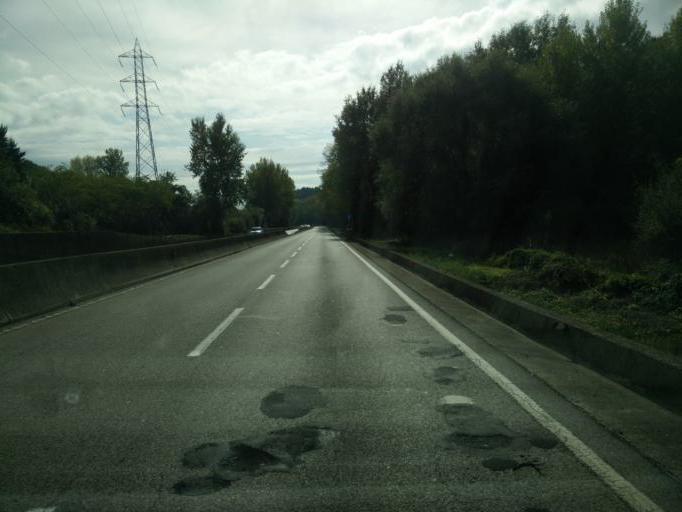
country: IT
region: Tuscany
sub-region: Provincia di Siena
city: Siena
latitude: 43.3210
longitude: 11.2997
